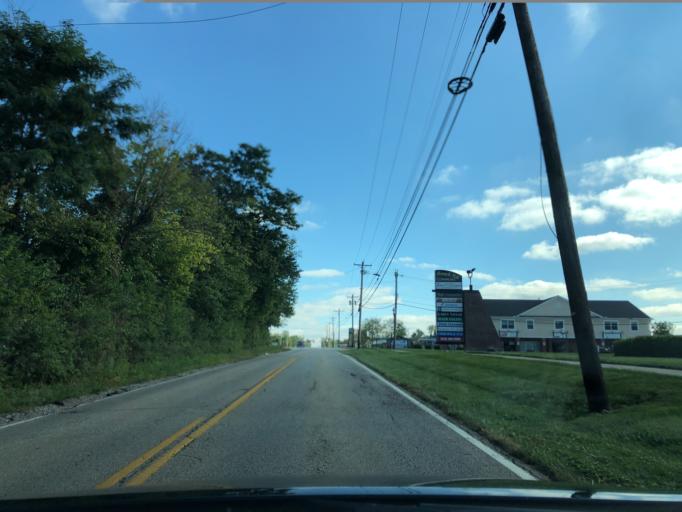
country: US
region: Ohio
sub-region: Hamilton County
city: Loveland
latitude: 39.2314
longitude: -84.2589
